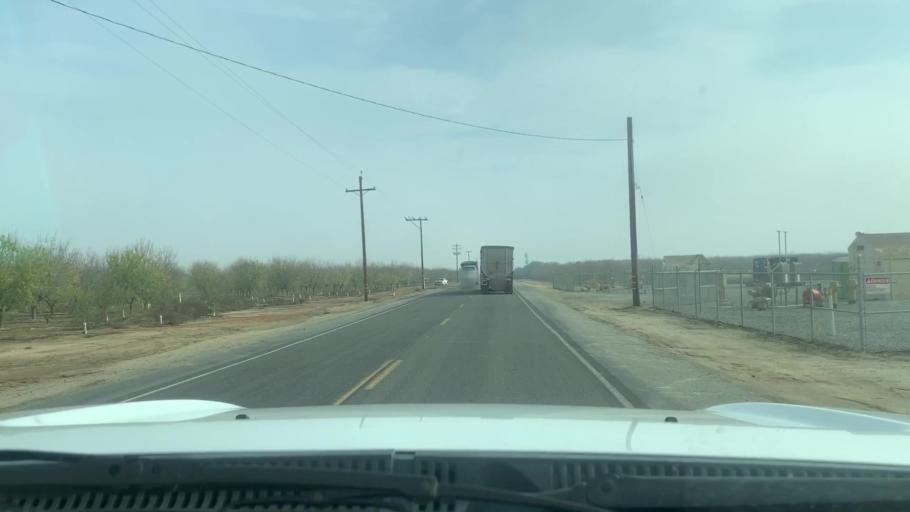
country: US
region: California
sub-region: Kern County
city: Buttonwillow
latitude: 35.5004
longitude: -119.4201
